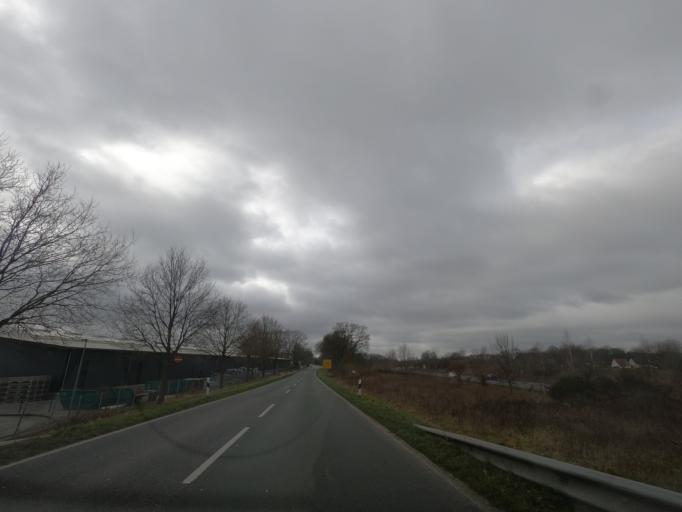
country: DE
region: Lower Saxony
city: Lastrup
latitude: 52.8031
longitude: 7.8814
